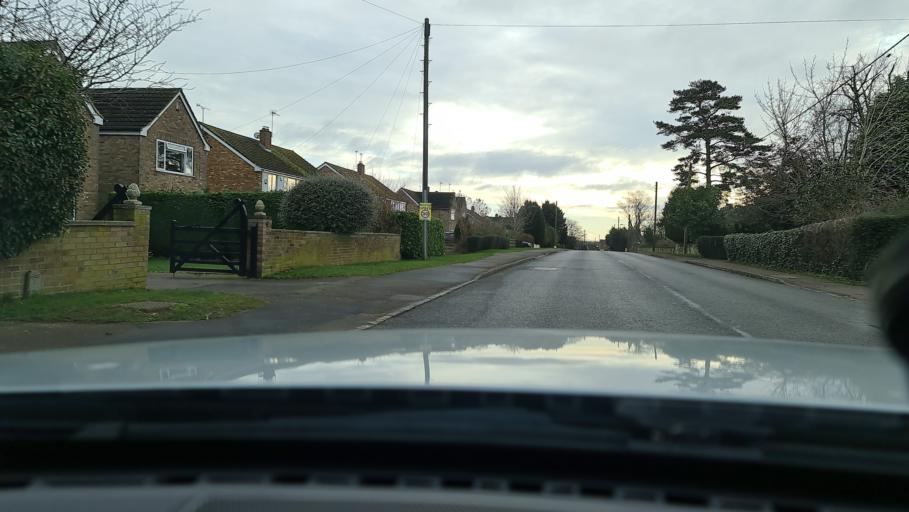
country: GB
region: England
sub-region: Oxfordshire
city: Banbury
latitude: 52.0791
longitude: -1.2738
